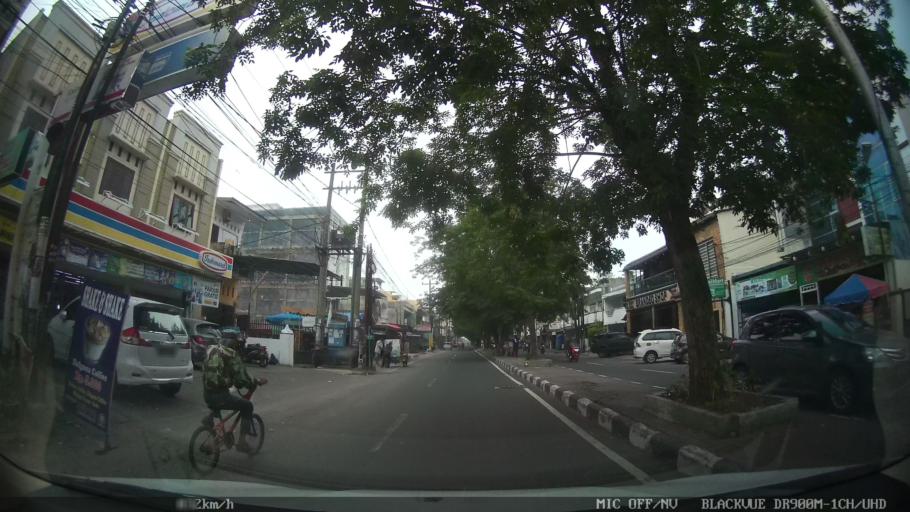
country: ID
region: North Sumatra
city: Medan
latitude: 3.5724
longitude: 98.6933
